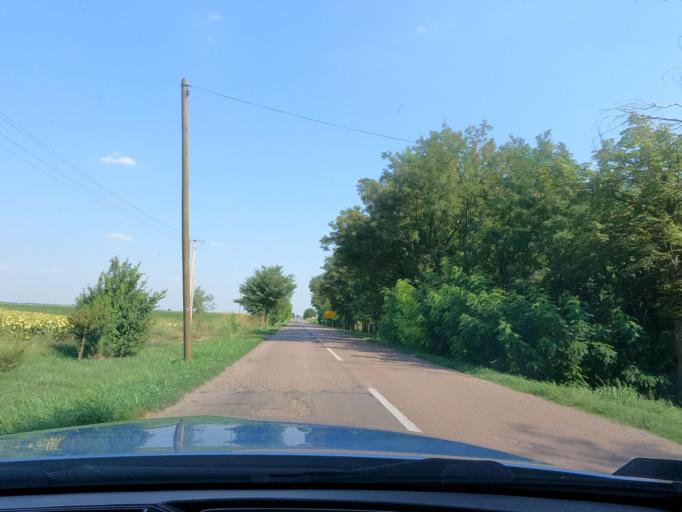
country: RS
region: Autonomna Pokrajina Vojvodina
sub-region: Severnobacki Okrug
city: Mali Igos
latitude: 45.7597
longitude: 19.7612
